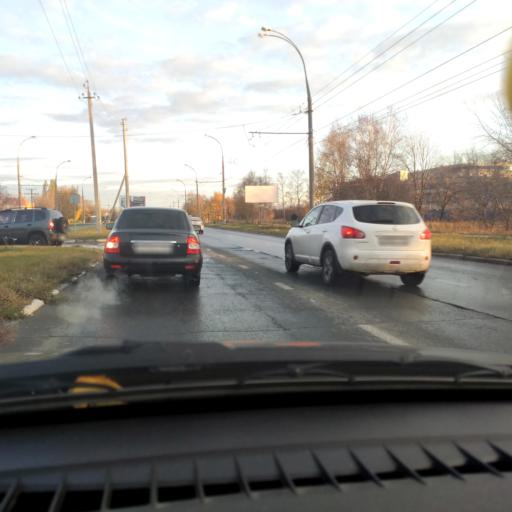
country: RU
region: Samara
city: Tol'yatti
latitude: 53.5410
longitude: 49.3004
